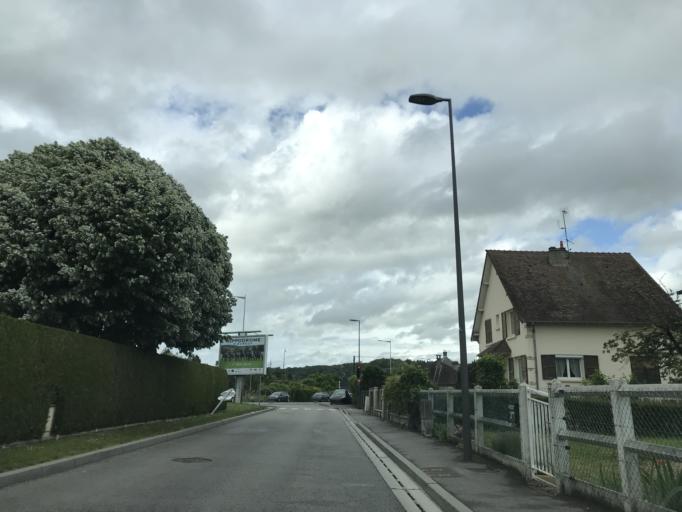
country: FR
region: Haute-Normandie
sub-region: Departement de l'Eure
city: Arnieres-sur-Iton
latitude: 49.0183
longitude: 1.1179
